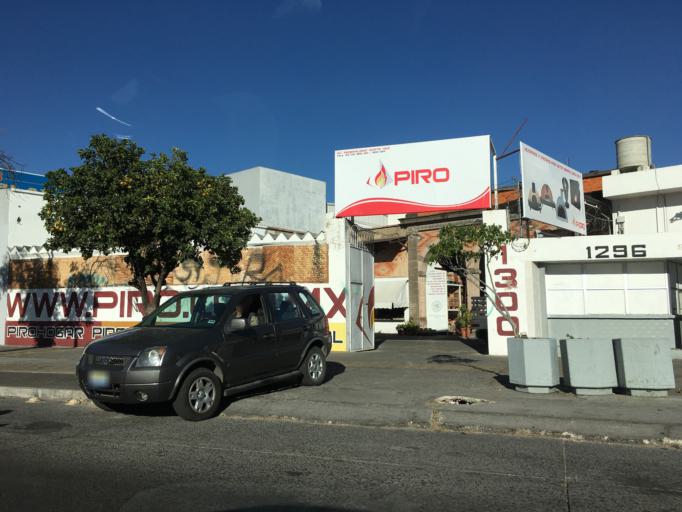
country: MX
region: Jalisco
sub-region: Zapopan
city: Zapopan
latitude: 20.6953
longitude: -103.3547
